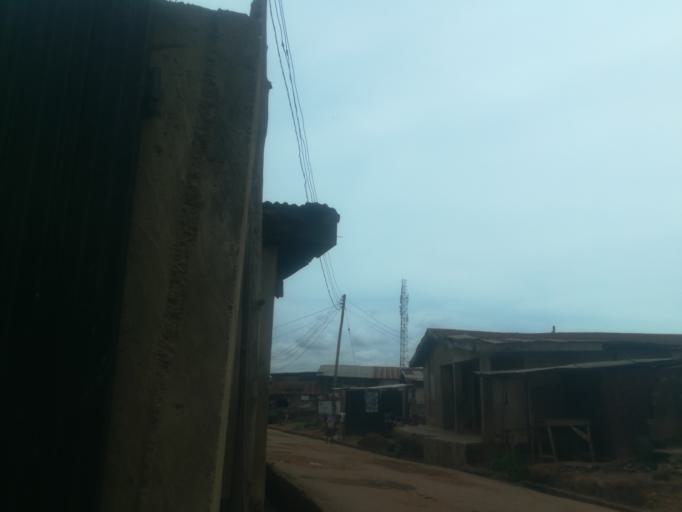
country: NG
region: Oyo
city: Ibadan
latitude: 7.3775
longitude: 3.9465
